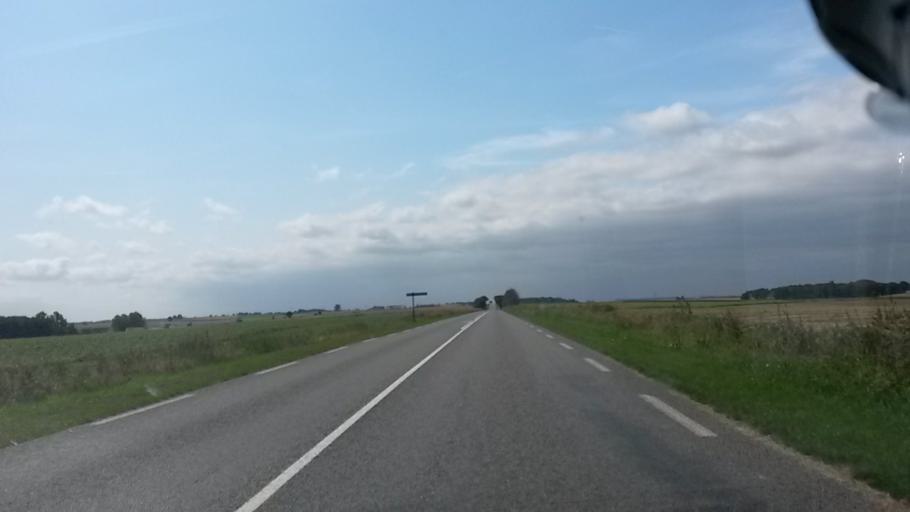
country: FR
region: Nord-Pas-de-Calais
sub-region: Departement du Pas-de-Calais
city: Hermies
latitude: 50.1300
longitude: 2.9836
